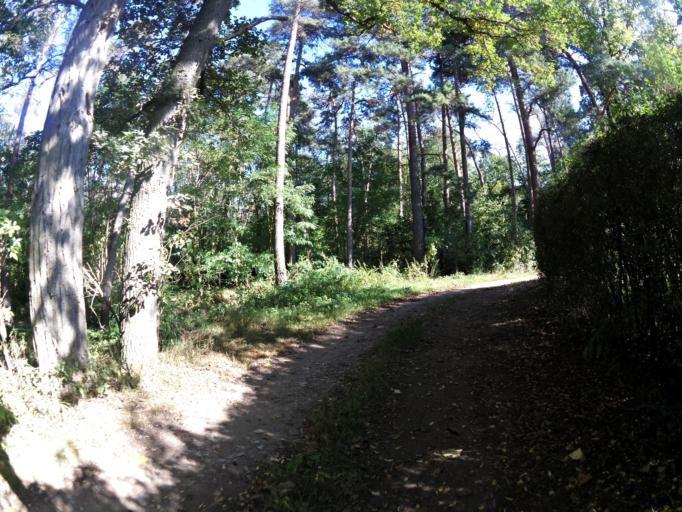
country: DE
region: Bavaria
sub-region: Regierungsbezirk Unterfranken
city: Sommerhausen
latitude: 49.6926
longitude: 10.0412
